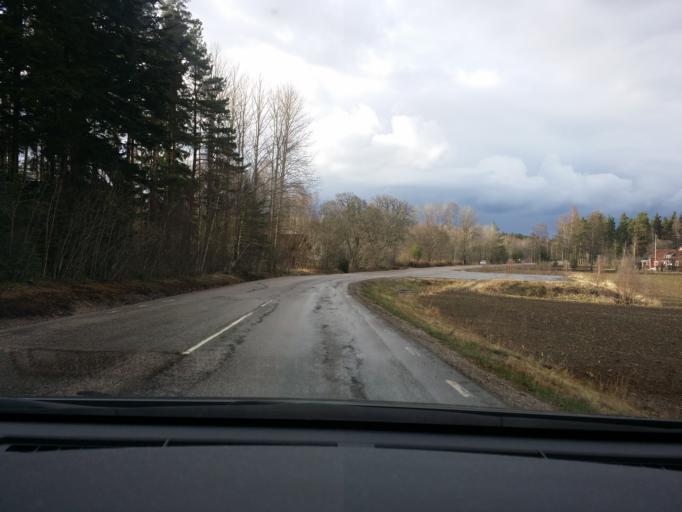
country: SE
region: Soedermanland
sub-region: Eskilstuna Kommun
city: Arla
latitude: 59.3177
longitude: 16.6807
